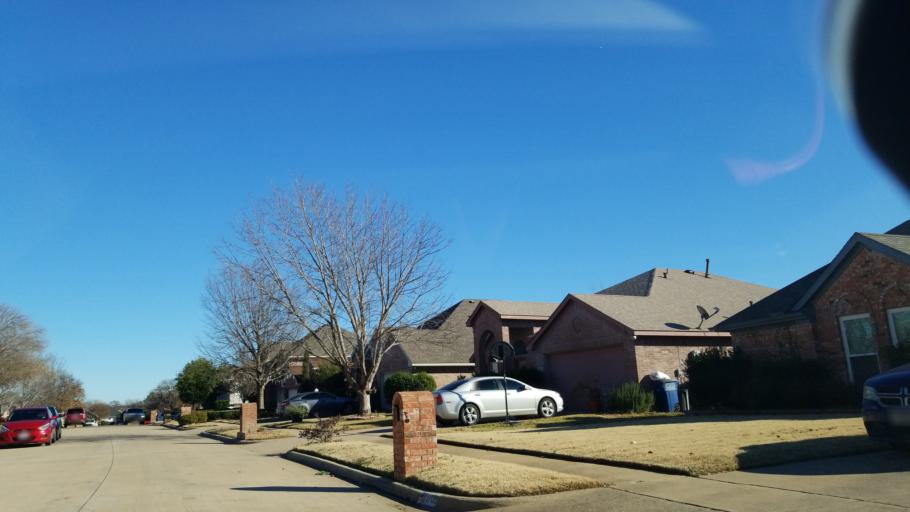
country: US
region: Texas
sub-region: Denton County
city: Corinth
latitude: 33.1383
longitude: -97.0841
